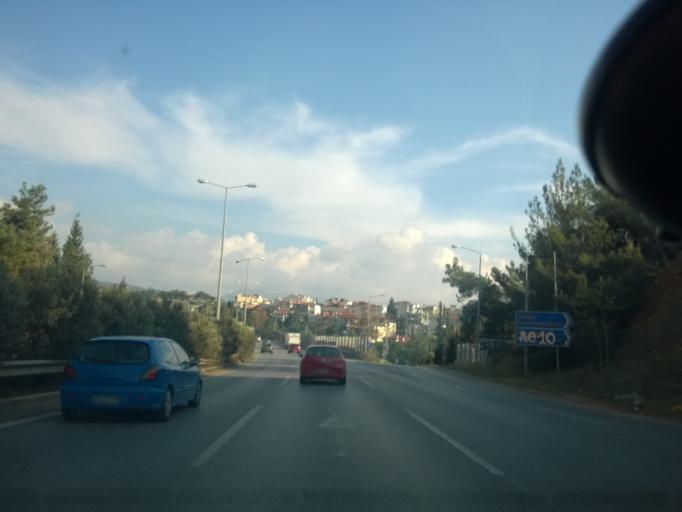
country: GR
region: Central Macedonia
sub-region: Nomos Thessalonikis
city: Triandria
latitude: 40.6140
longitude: 22.9890
